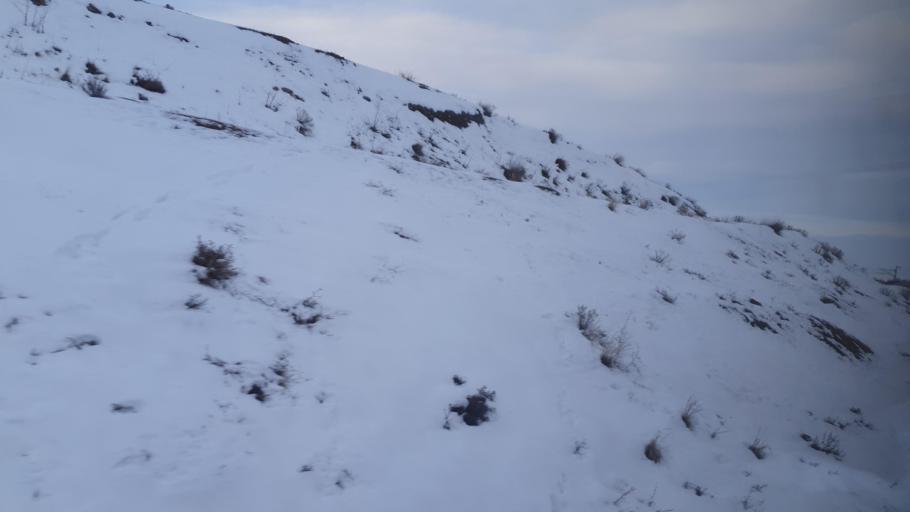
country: TR
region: Yozgat
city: Yerkoy
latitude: 39.6869
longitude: 34.4131
